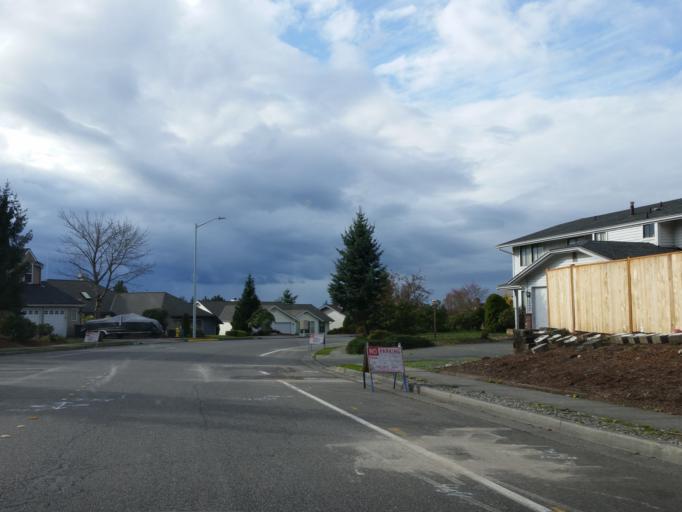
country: US
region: Washington
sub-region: Snohomish County
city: Lynnwood
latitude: 47.8295
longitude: -122.3262
